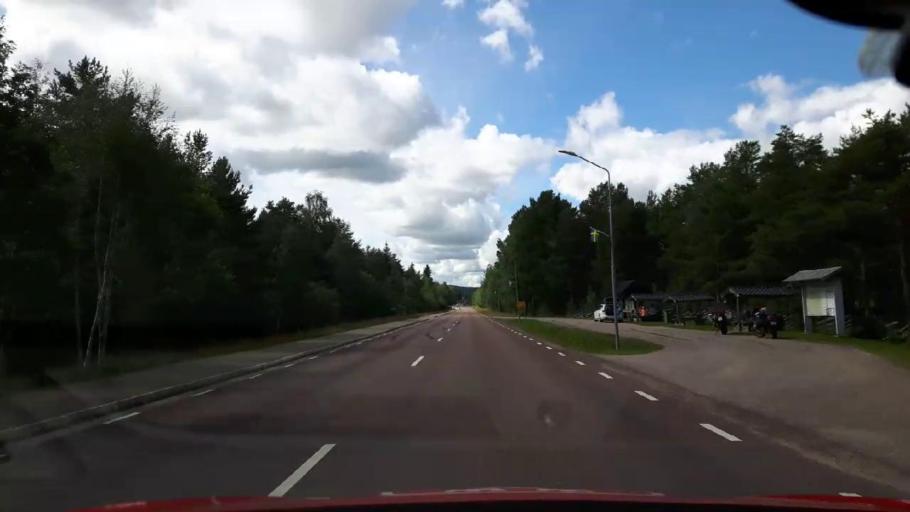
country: SE
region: Jaemtland
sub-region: Harjedalens Kommun
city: Sveg
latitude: 61.8560
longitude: 14.0901
